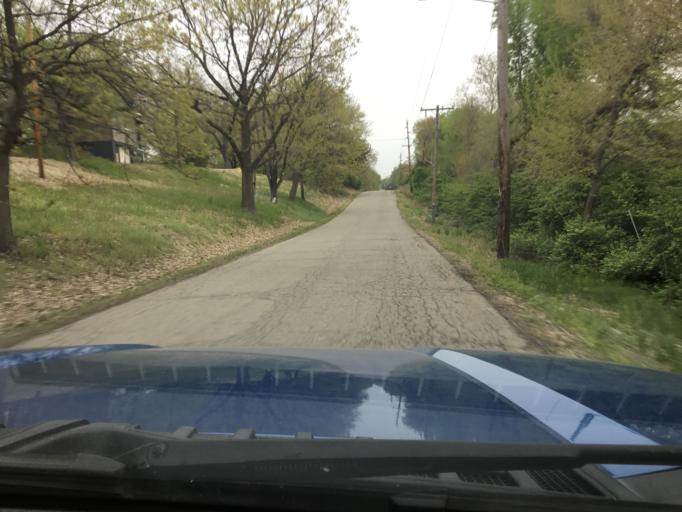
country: US
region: Kansas
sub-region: Shawnee County
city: Topeka
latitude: 39.1021
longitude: -95.6816
